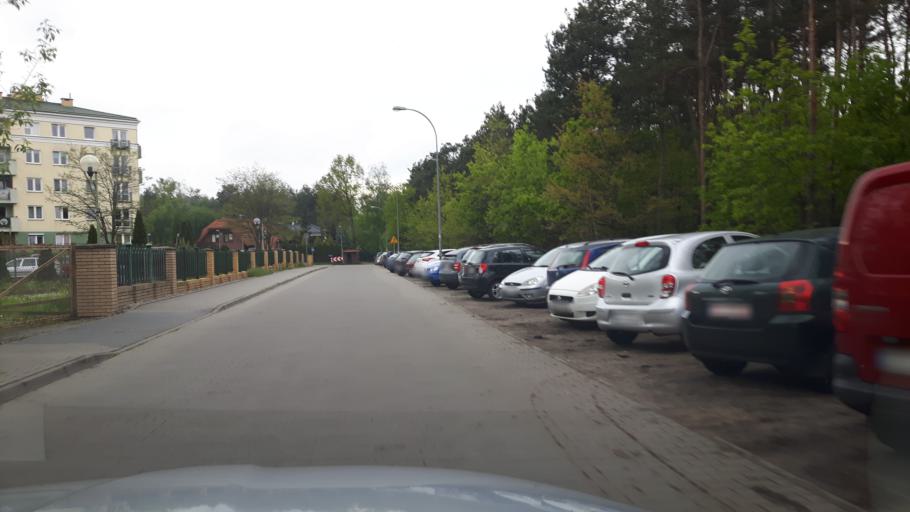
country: PL
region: Masovian Voivodeship
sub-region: Warszawa
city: Rembertow
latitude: 52.2743
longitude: 21.1547
